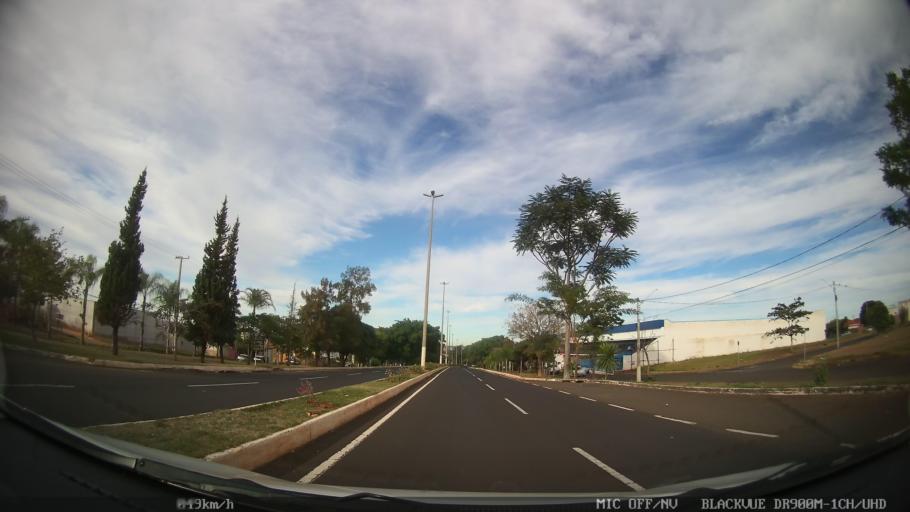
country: BR
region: Sao Paulo
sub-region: Catanduva
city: Catanduva
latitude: -21.1140
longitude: -48.9630
